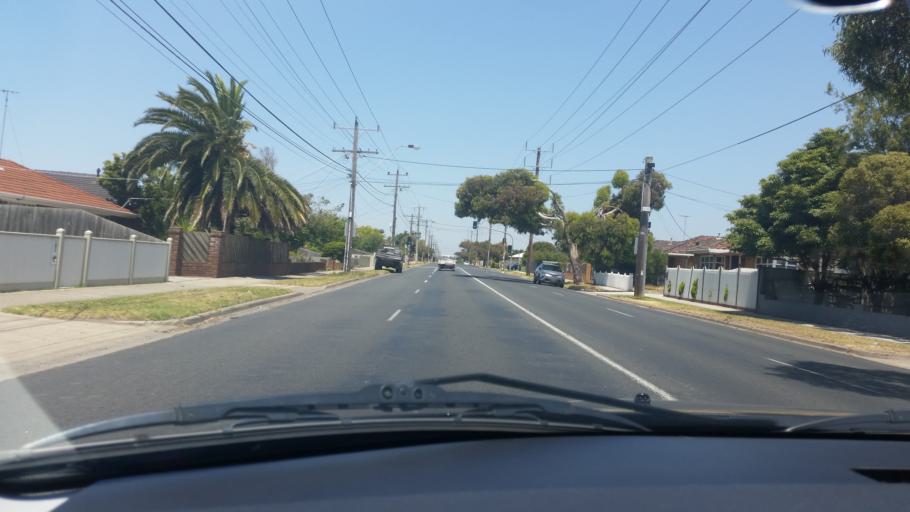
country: AU
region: Victoria
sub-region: Greater Geelong
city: Bell Park
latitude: -38.1128
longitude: 144.3430
